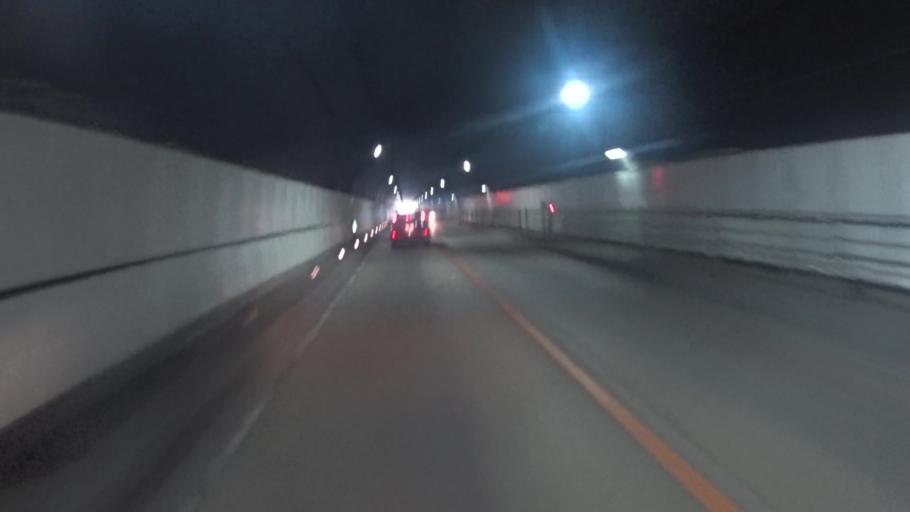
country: JP
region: Nara
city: Nara-shi
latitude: 34.7602
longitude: 135.9468
